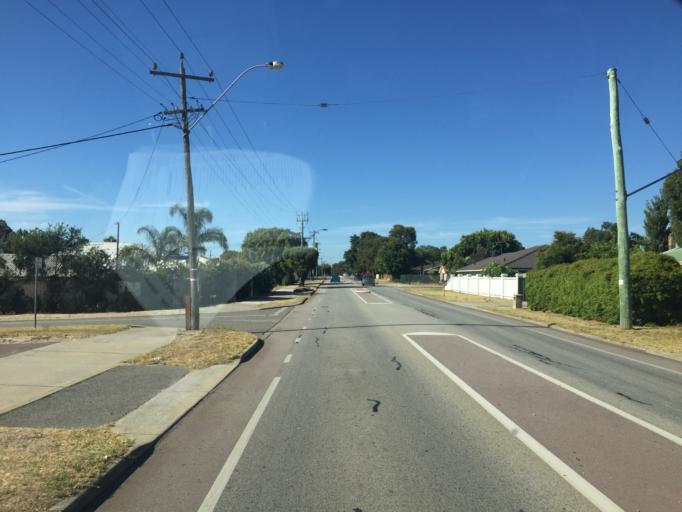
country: AU
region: Western Australia
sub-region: Gosnells
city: Maddington
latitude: -32.0383
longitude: 115.9821
